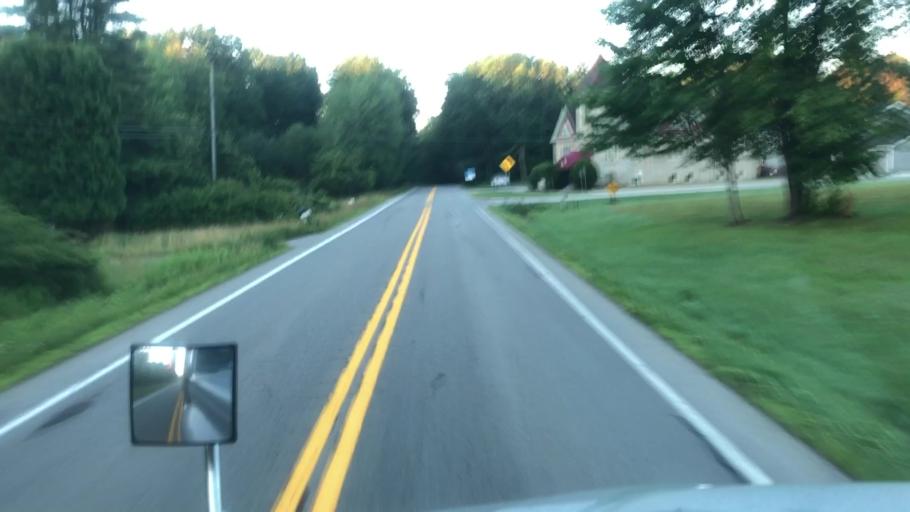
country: US
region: Pennsylvania
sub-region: Crawford County
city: Titusville
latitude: 41.5697
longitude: -79.6104
